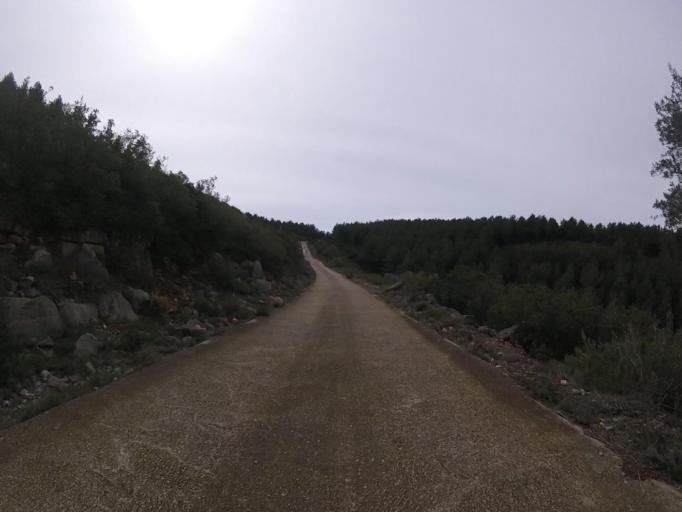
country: ES
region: Valencia
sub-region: Provincia de Castello
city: Cabanes
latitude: 40.1902
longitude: 0.0788
